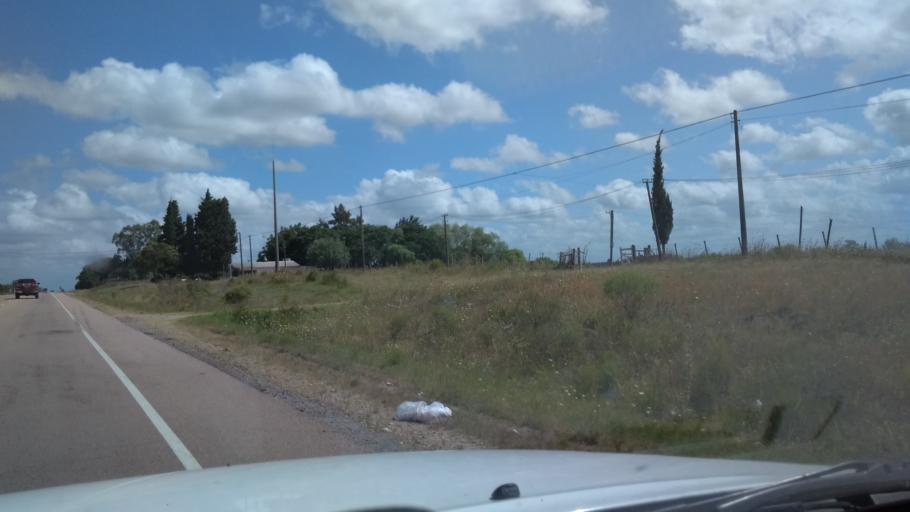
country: UY
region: Canelones
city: Sauce
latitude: -34.6239
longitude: -56.0505
